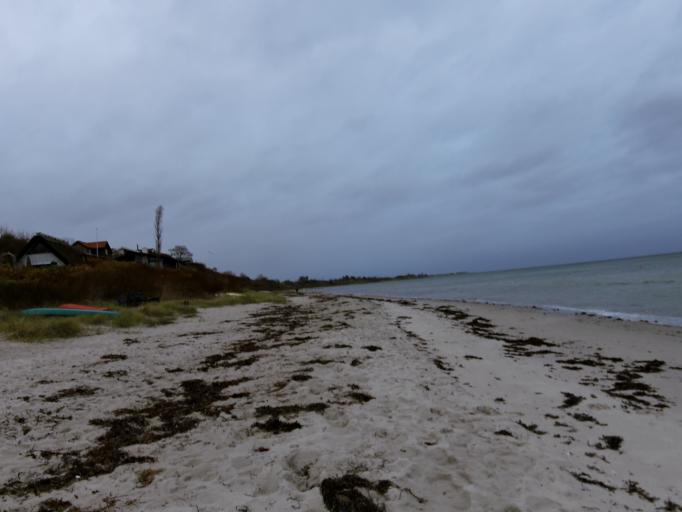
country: DK
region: Central Jutland
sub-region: Arhus Kommune
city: Malling
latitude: 55.9864
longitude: 10.2525
